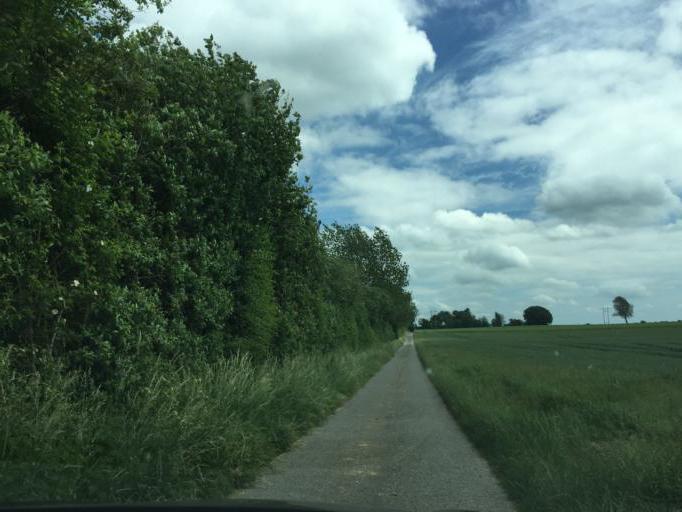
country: DK
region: South Denmark
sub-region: Faaborg-Midtfyn Kommune
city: Ringe
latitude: 55.1998
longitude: 10.4356
